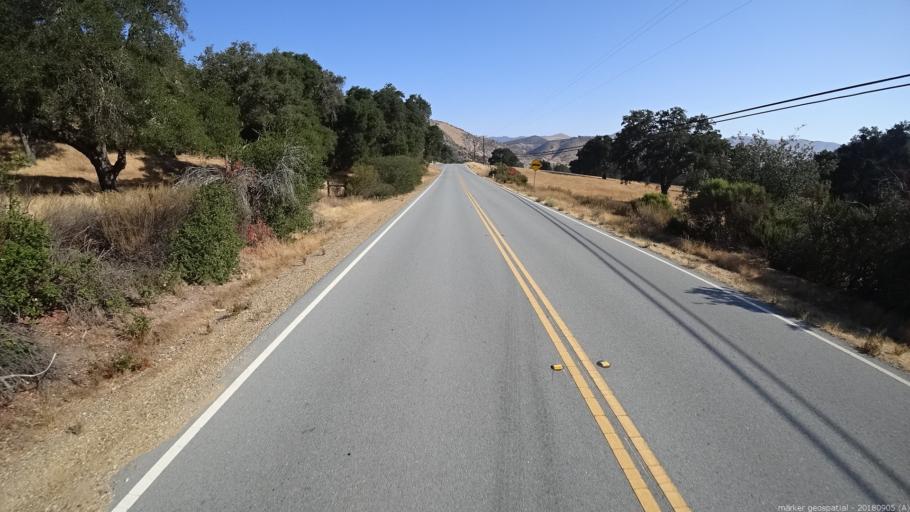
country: US
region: California
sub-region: Monterey County
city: Greenfield
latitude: 36.2446
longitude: -121.4324
